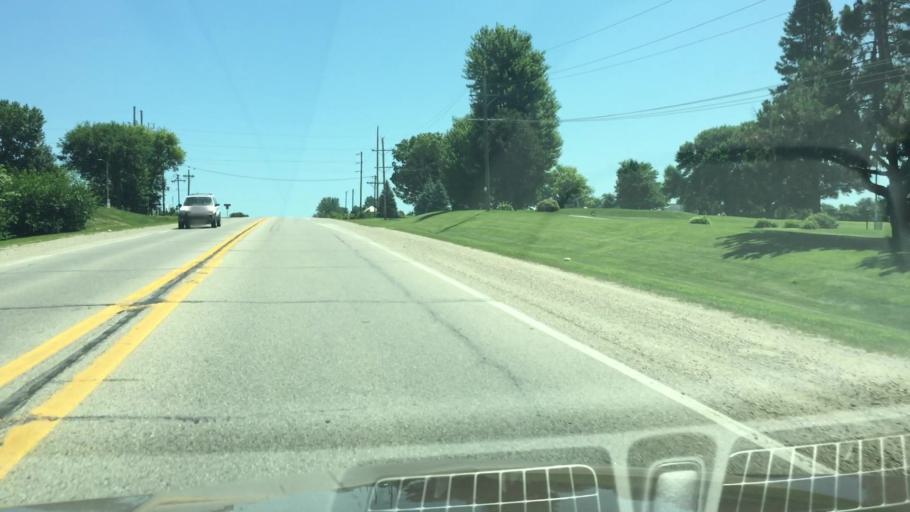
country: US
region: Iowa
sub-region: Linn County
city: Mount Vernon
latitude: 41.9169
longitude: -91.4073
